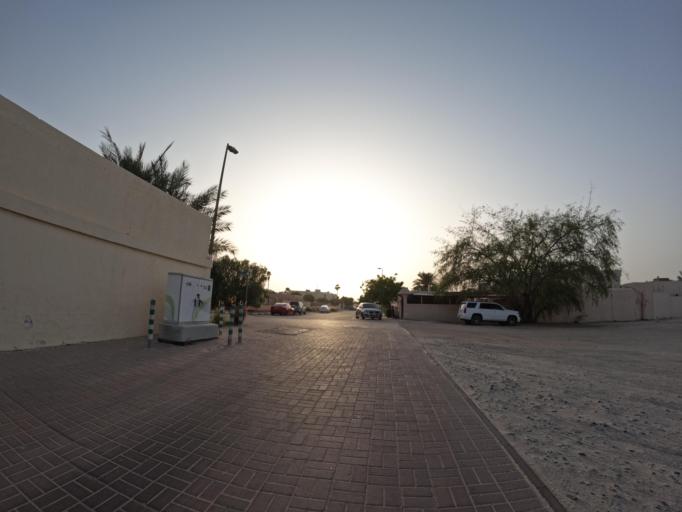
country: AE
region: Dubai
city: Dubai
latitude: 25.1943
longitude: 55.2441
